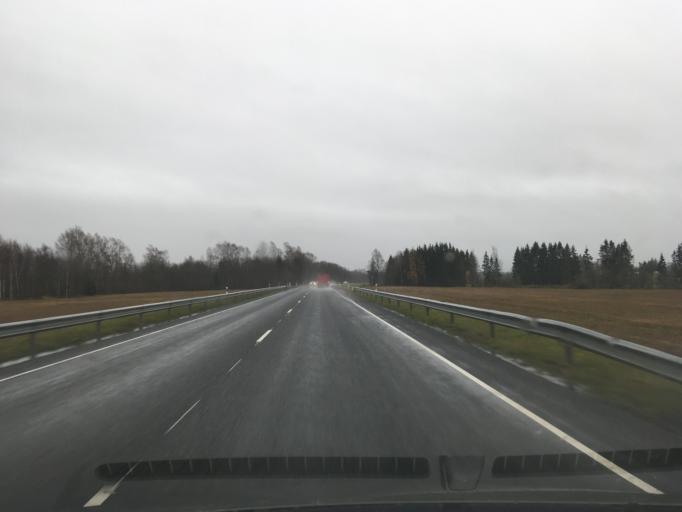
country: EE
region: Harju
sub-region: Nissi vald
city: Turba
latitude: 58.9284
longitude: 24.1055
